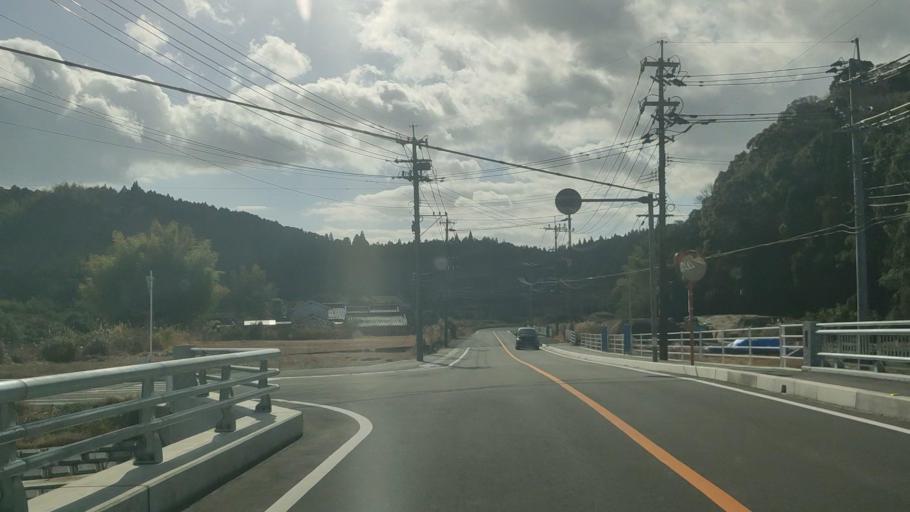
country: JP
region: Kagoshima
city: Okuchi-shinohara
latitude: 31.9415
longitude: 130.7098
